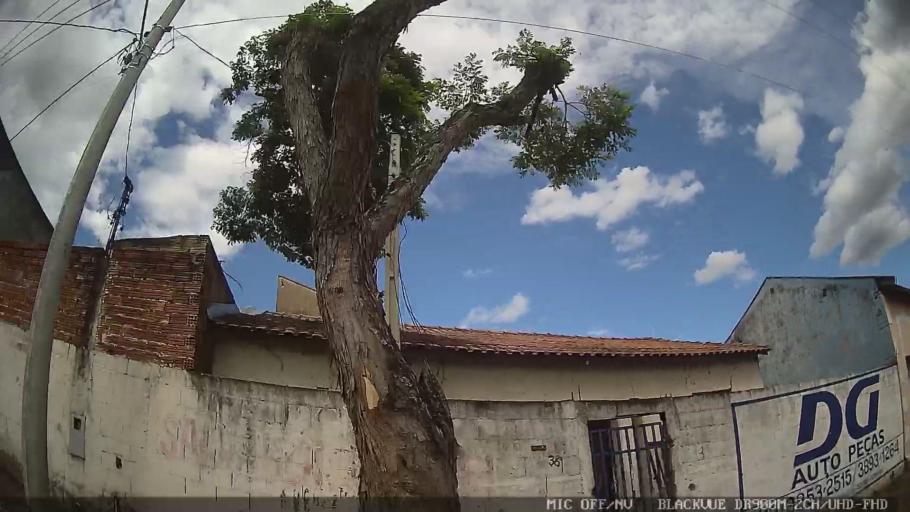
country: BR
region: Sao Paulo
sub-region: Pedreira
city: Pedreira
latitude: -22.7428
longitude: -46.9134
